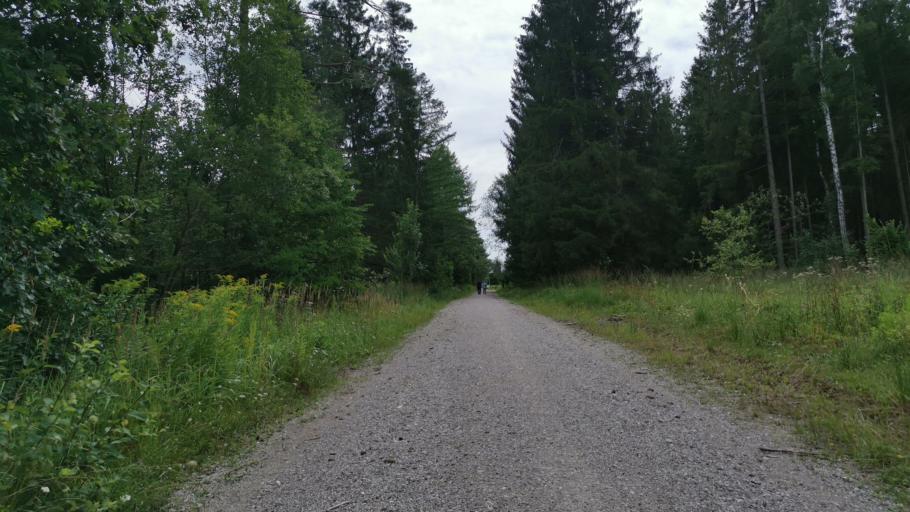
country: DE
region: Bavaria
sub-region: Upper Bavaria
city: Unterhaching
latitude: 48.0729
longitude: 11.5768
